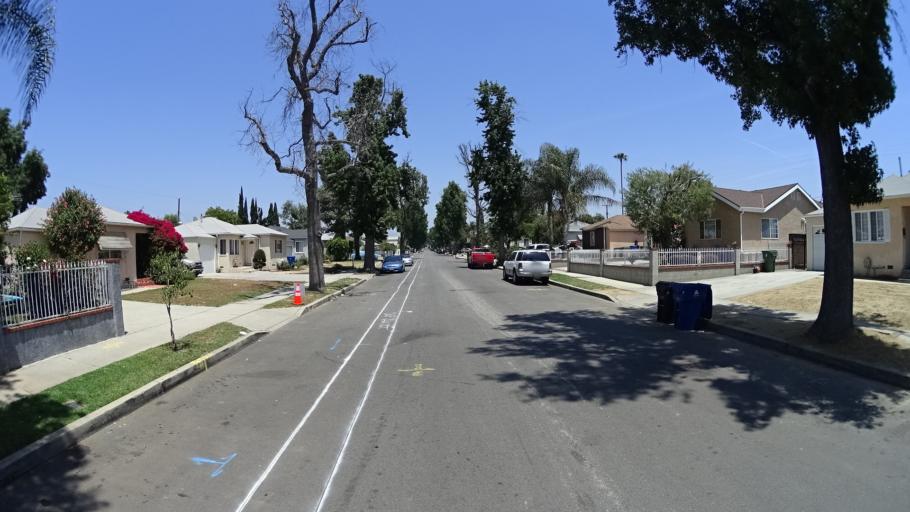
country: US
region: California
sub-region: Los Angeles County
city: Van Nuys
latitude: 34.2156
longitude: -118.4627
